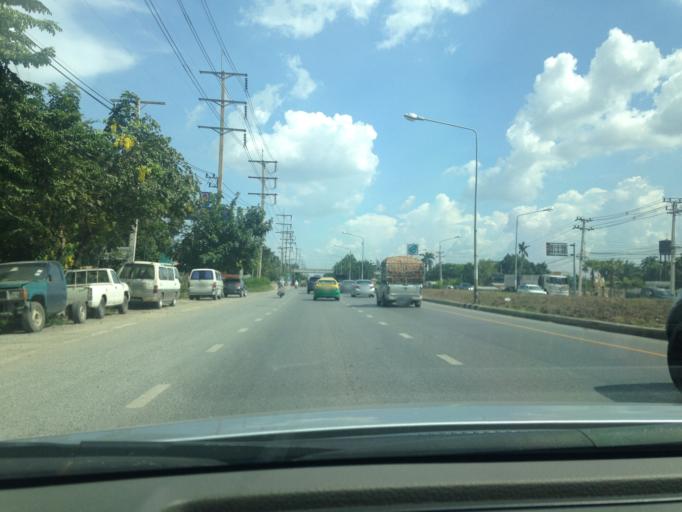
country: TH
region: Phra Nakhon Si Ayutthaya
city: Ban Bang Kadi Pathum Thani
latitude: 13.9960
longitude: 100.5758
